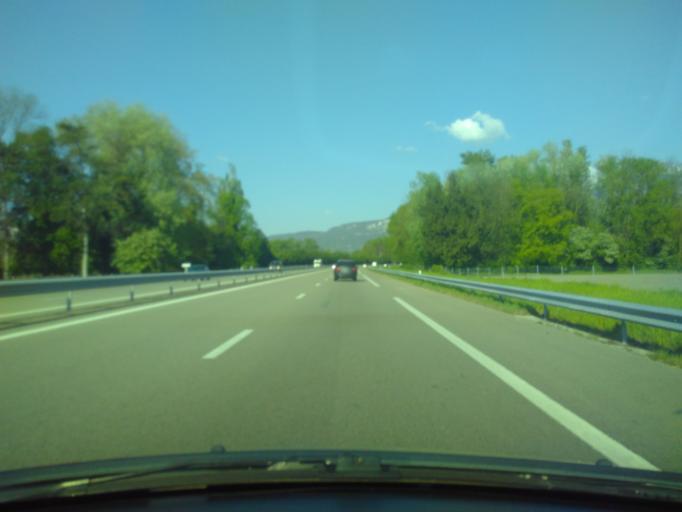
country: FR
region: Rhone-Alpes
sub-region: Departement de l'Isere
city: Saint-Quentin-sur-Isere
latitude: 45.2966
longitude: 5.5588
